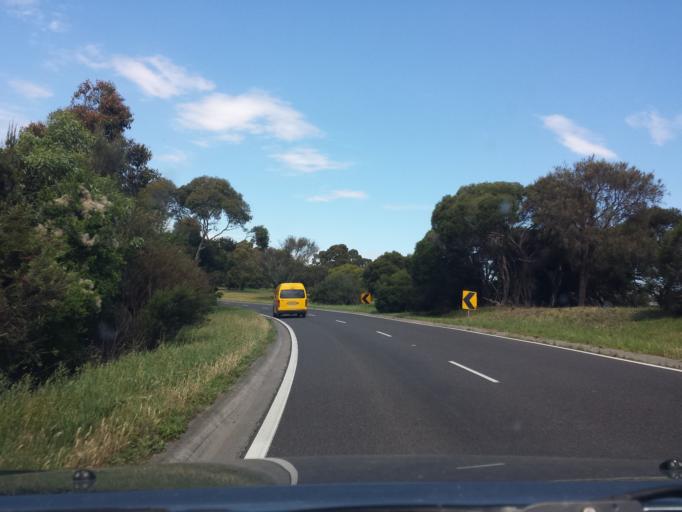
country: AU
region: Victoria
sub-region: Monash
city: Mulgrave
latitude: -37.9183
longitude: 145.1721
